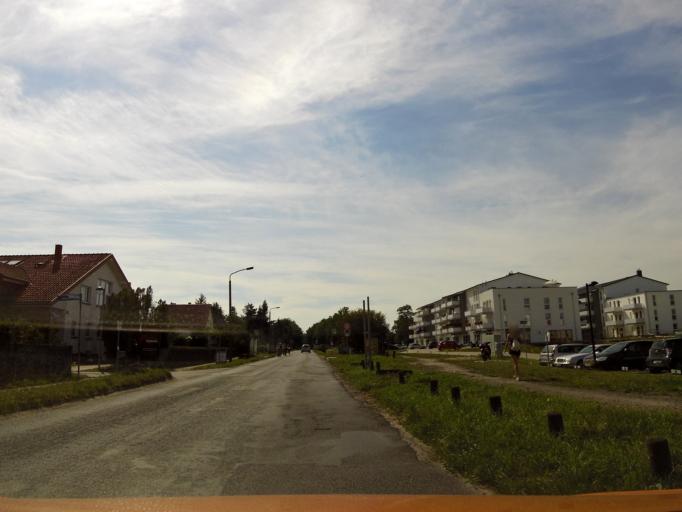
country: DE
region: Brandenburg
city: Teltow
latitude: 52.3860
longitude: 13.2637
